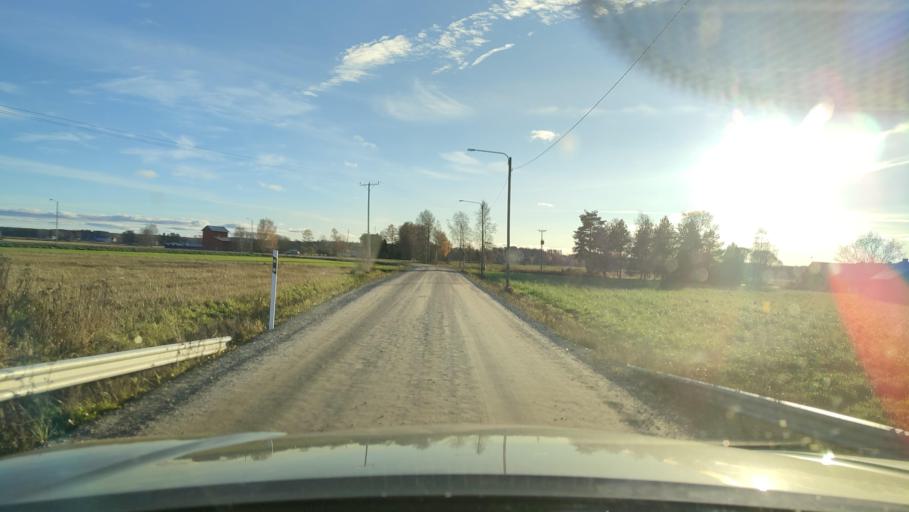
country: FI
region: Ostrobothnia
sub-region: Vaasa
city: Teeriniemi
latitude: 63.0106
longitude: 21.6926
